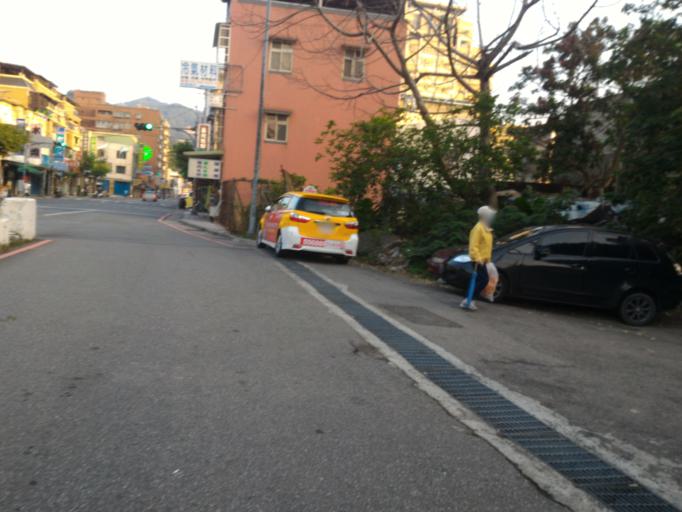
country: TW
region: Taiwan
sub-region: Taoyuan
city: Taoyuan
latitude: 24.9696
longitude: 121.3935
